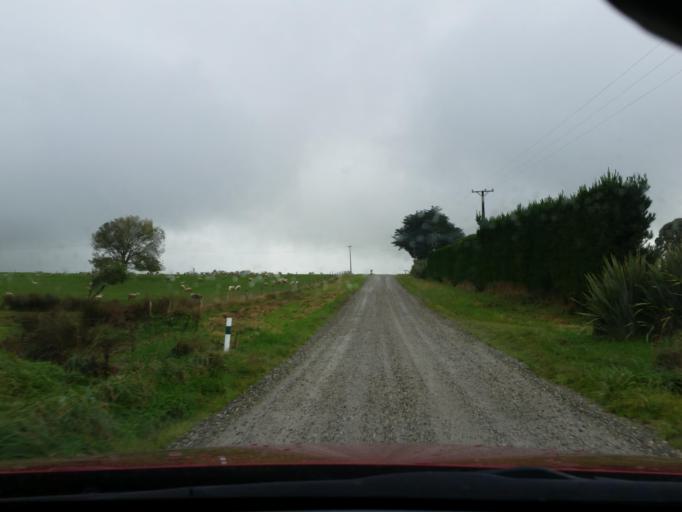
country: NZ
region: Southland
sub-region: Invercargill City
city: Invercargill
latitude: -46.2818
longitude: 168.5563
